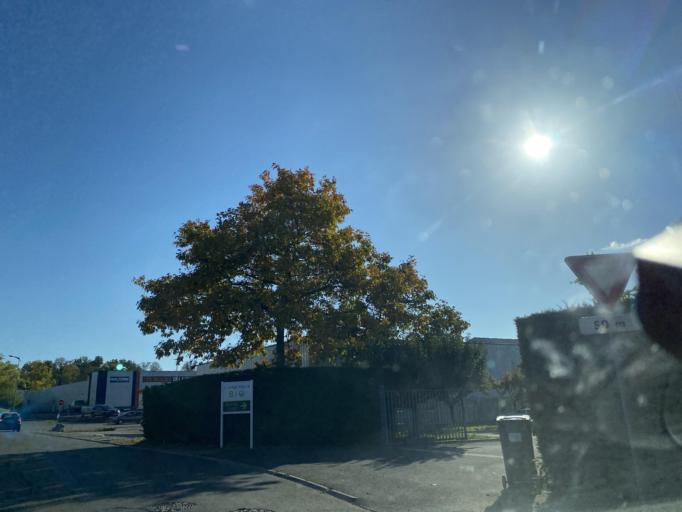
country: FR
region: Auvergne
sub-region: Departement du Puy-de-Dome
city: Peschadoires
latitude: 45.8398
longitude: 3.5108
